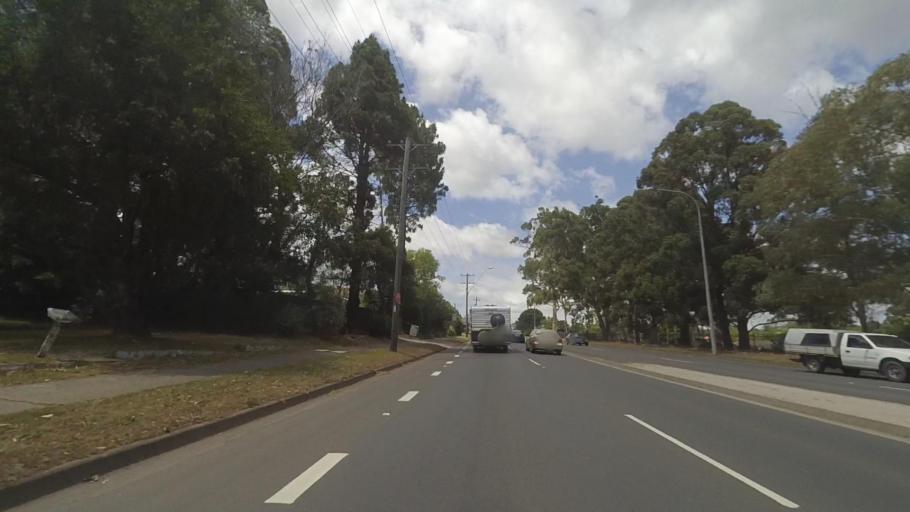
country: AU
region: New South Wales
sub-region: Shoalhaven Shire
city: Nowra
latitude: -34.8798
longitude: 150.6045
